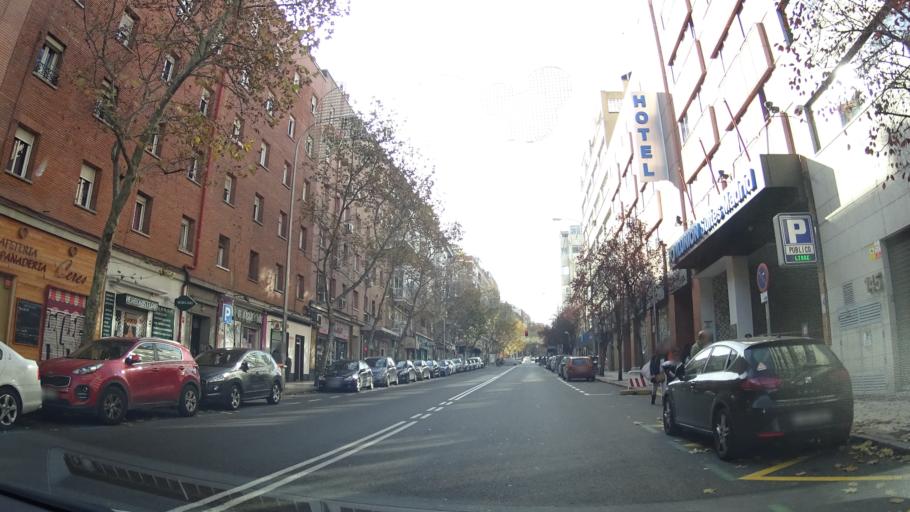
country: ES
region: Madrid
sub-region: Provincia de Madrid
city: Chamartin
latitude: 40.4479
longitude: -3.6688
